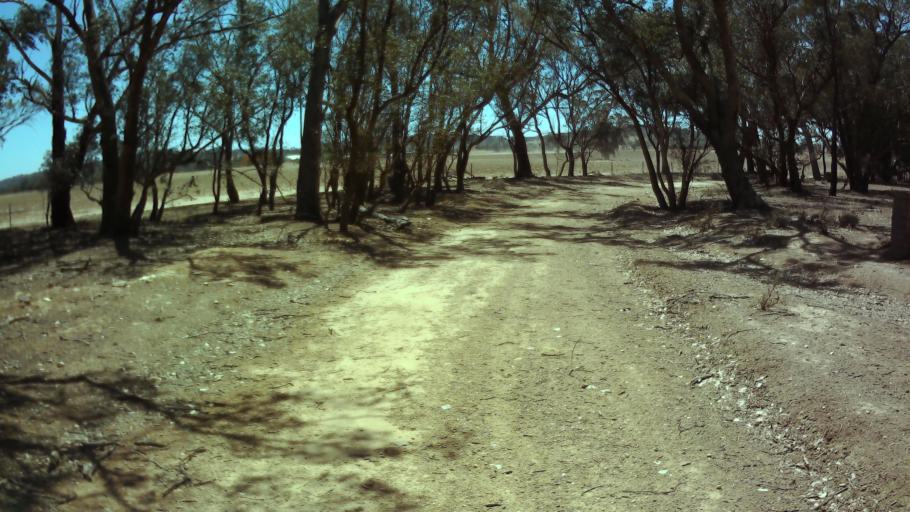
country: AU
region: New South Wales
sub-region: Weddin
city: Grenfell
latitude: -33.9791
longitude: 148.1694
